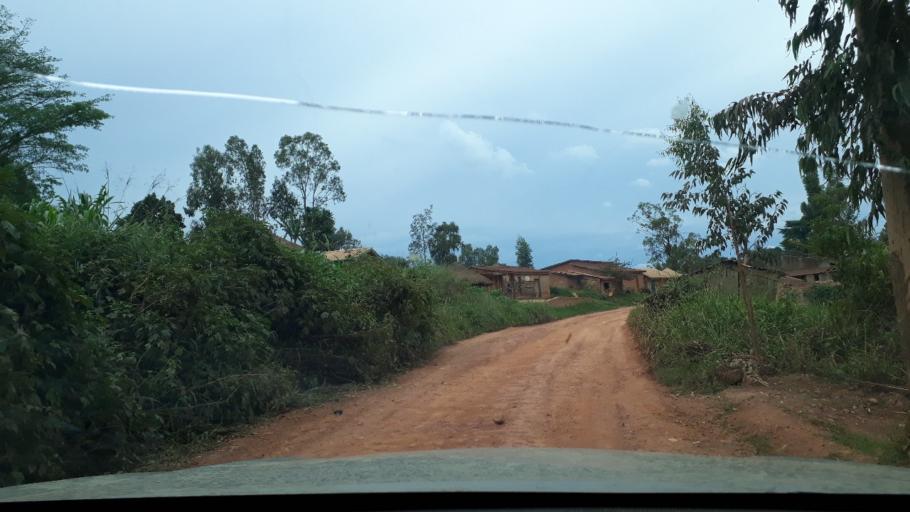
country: CD
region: Eastern Province
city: Bunia
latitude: 1.7864
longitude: 30.3873
